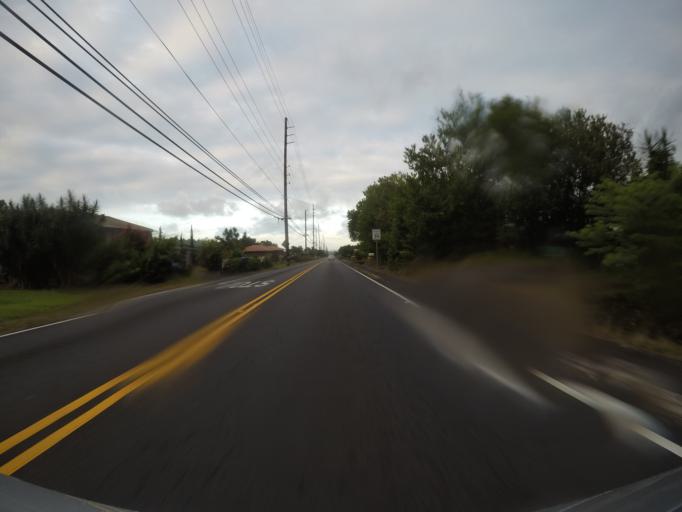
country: US
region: Hawaii
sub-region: Hawaii County
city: Hilo
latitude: 19.6830
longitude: -155.0896
